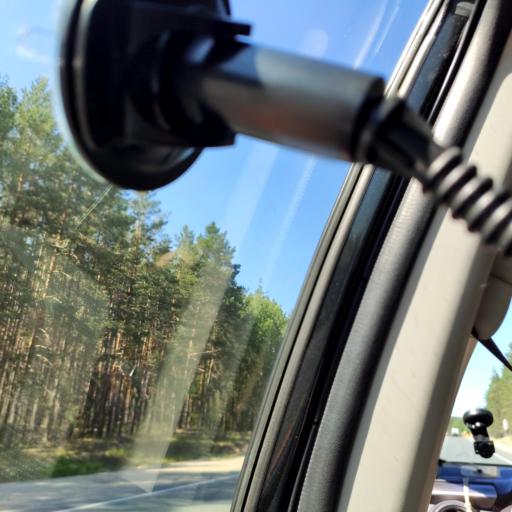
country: RU
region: Mariy-El
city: Krasnogorskiy
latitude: 56.1105
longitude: 48.3451
